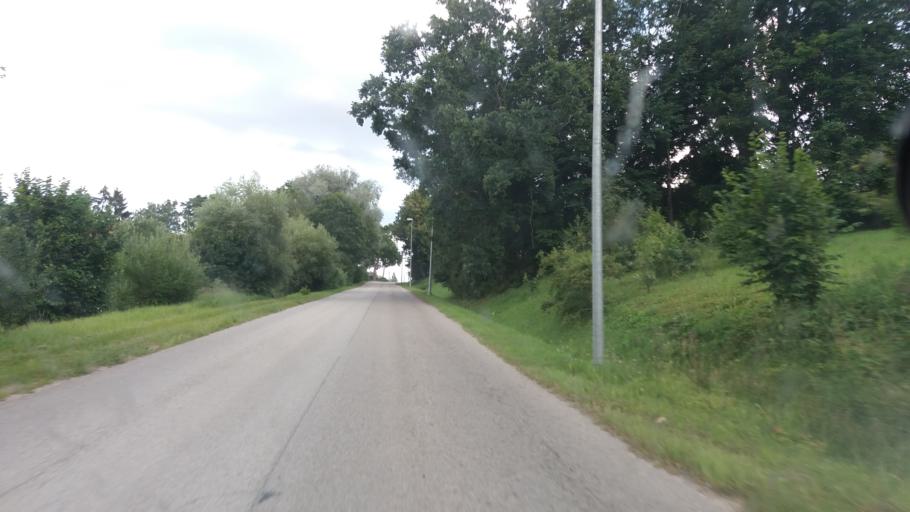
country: LV
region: Talsu Rajons
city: Sabile
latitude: 57.0391
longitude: 22.5702
